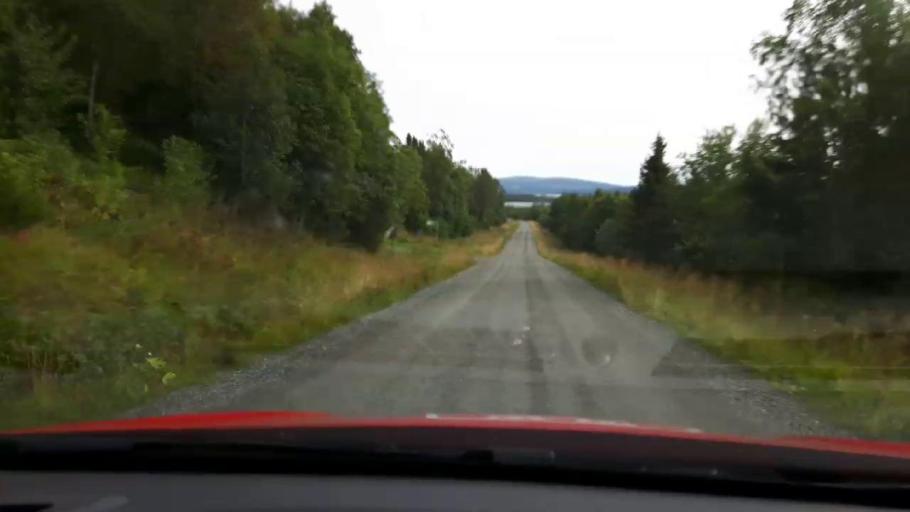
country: SE
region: Jaemtland
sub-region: Are Kommun
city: Are
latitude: 63.7471
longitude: 12.9693
